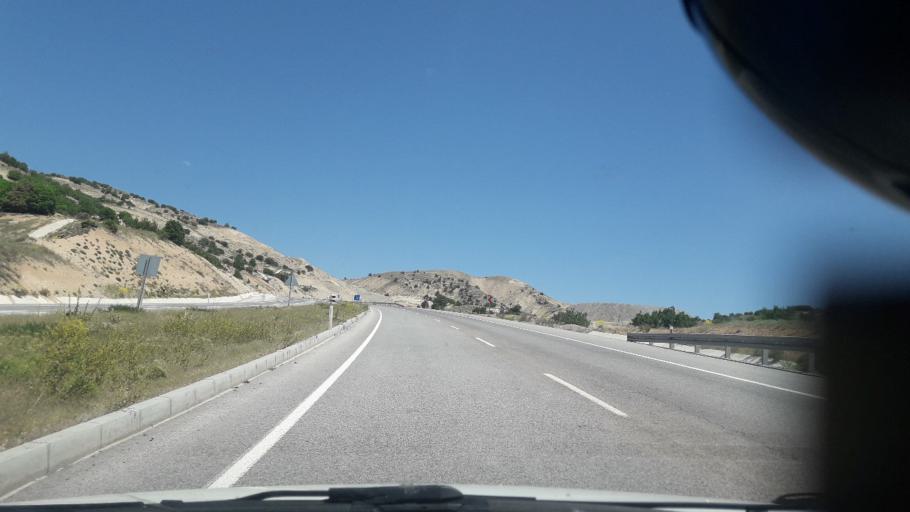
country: TR
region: Malatya
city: Hekimhan
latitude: 38.7389
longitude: 38.0004
